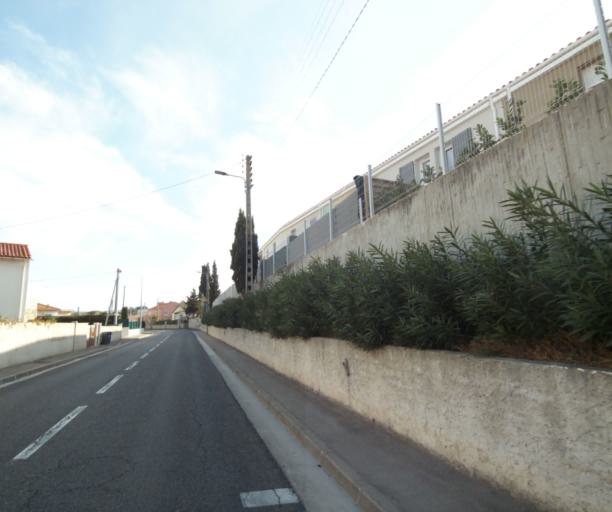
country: FR
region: Provence-Alpes-Cote d'Azur
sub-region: Departement des Bouches-du-Rhone
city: Chateauneuf-les-Martigues
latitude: 43.3818
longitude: 5.1682
